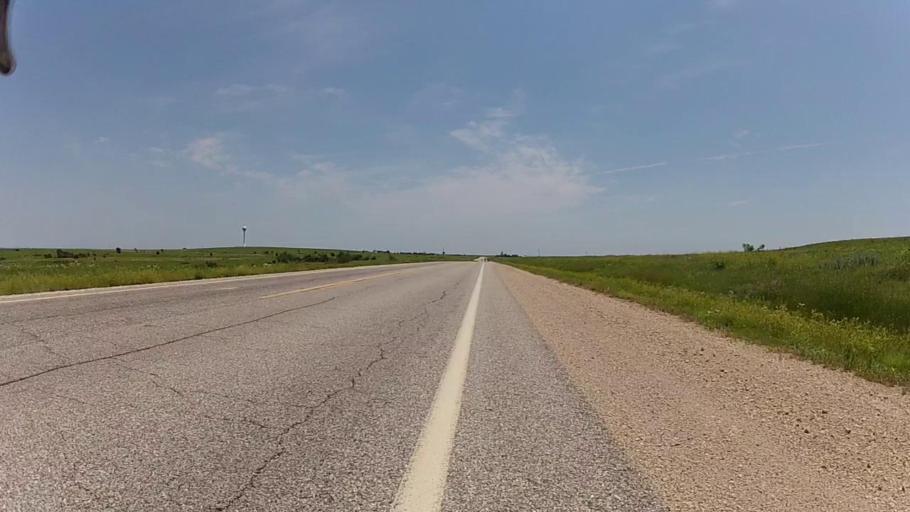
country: US
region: Kansas
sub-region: Chautauqua County
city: Sedan
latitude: 37.1096
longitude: -96.2533
